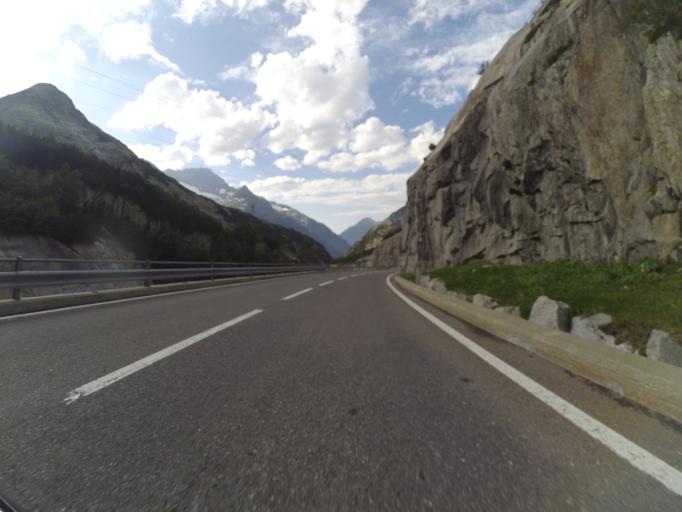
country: CH
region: Bern
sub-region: Interlaken-Oberhasli District
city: Meiringen
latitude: 46.5922
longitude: 8.3241
